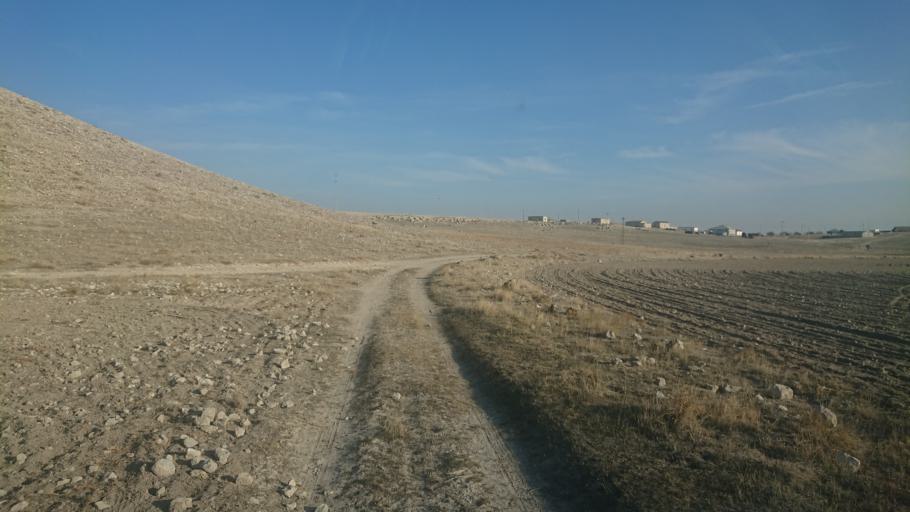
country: TR
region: Aksaray
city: Sultanhani
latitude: 38.1437
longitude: 33.5846
